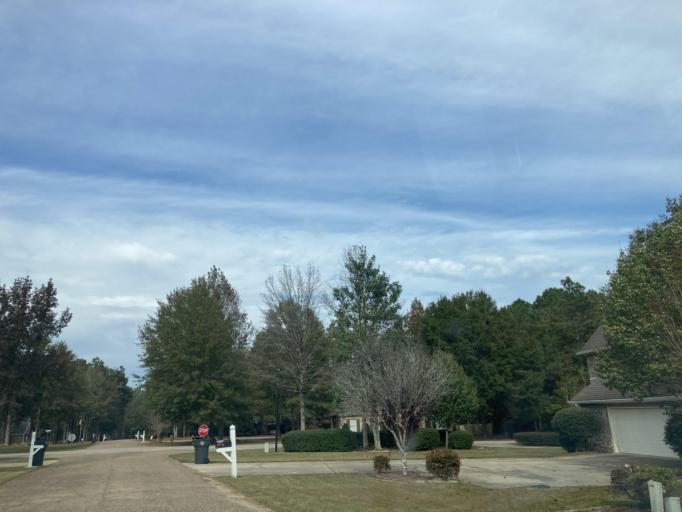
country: US
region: Mississippi
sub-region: Lamar County
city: West Hattiesburg
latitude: 31.3250
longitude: -89.4398
